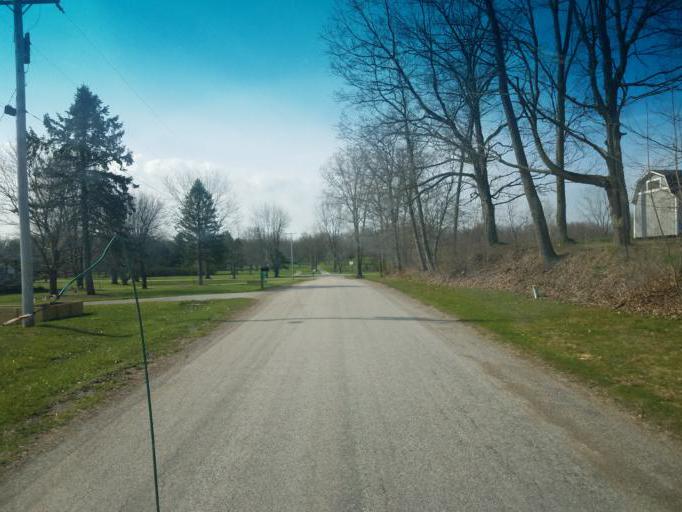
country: US
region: Ohio
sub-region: Richland County
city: Lincoln Heights
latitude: 40.8797
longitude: -82.5206
